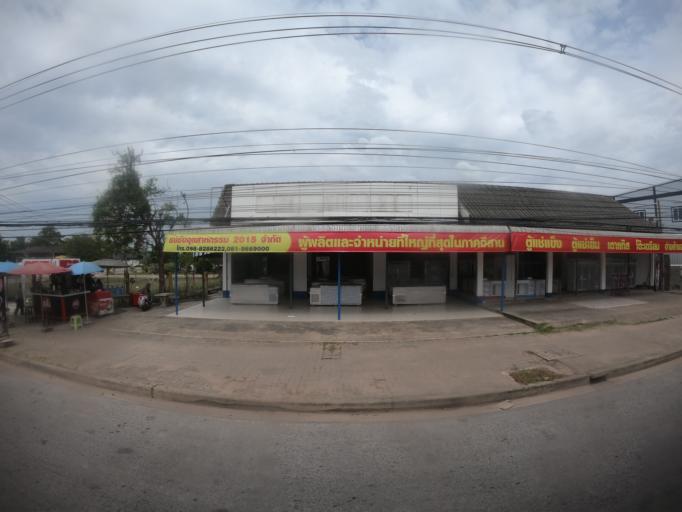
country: TH
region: Roi Et
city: Roi Et
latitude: 16.0607
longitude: 103.6264
